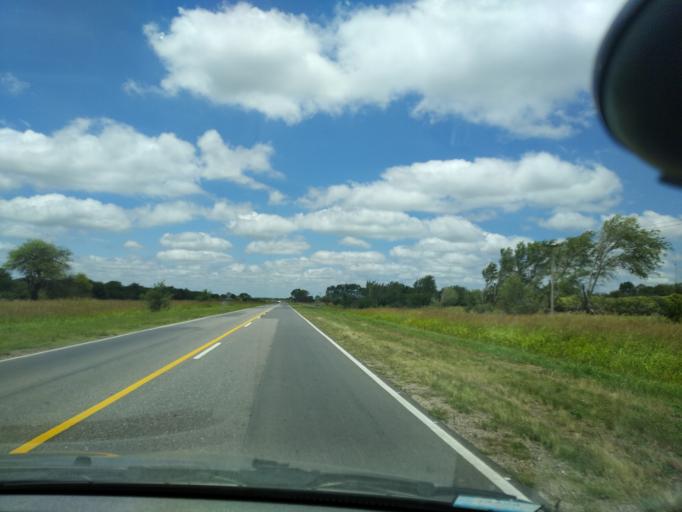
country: AR
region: Cordoba
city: Alta Gracia
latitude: -31.6526
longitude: -64.2867
